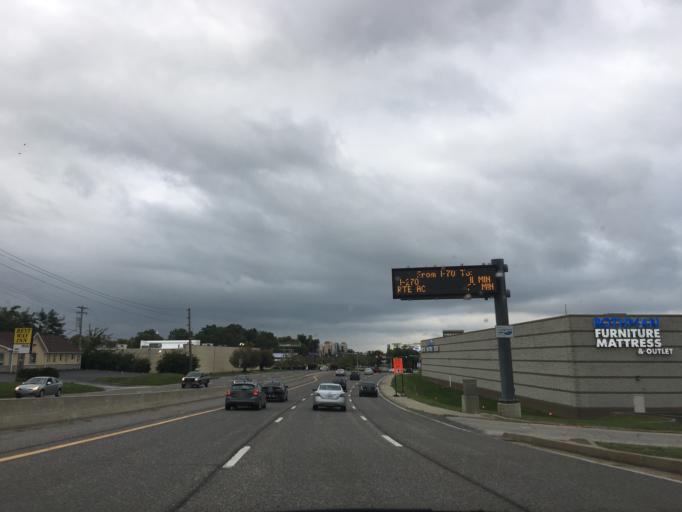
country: US
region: Missouri
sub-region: Saint Louis County
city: Saint Ann
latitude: 38.7331
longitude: -90.4038
